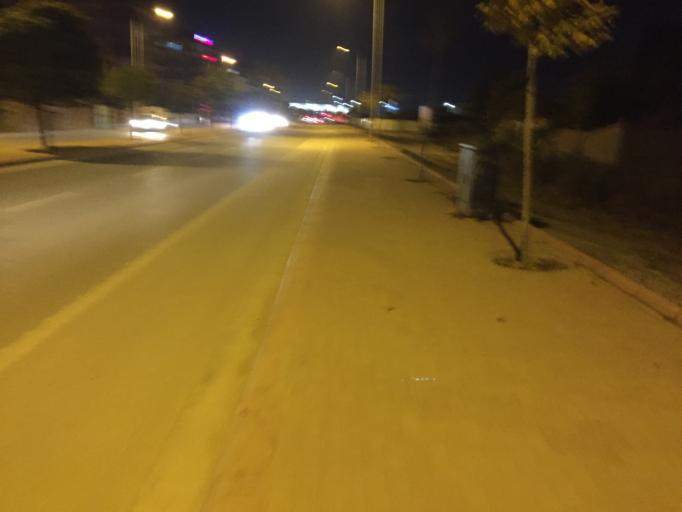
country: TR
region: Konya
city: Selcuklu
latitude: 37.8732
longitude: 32.5146
